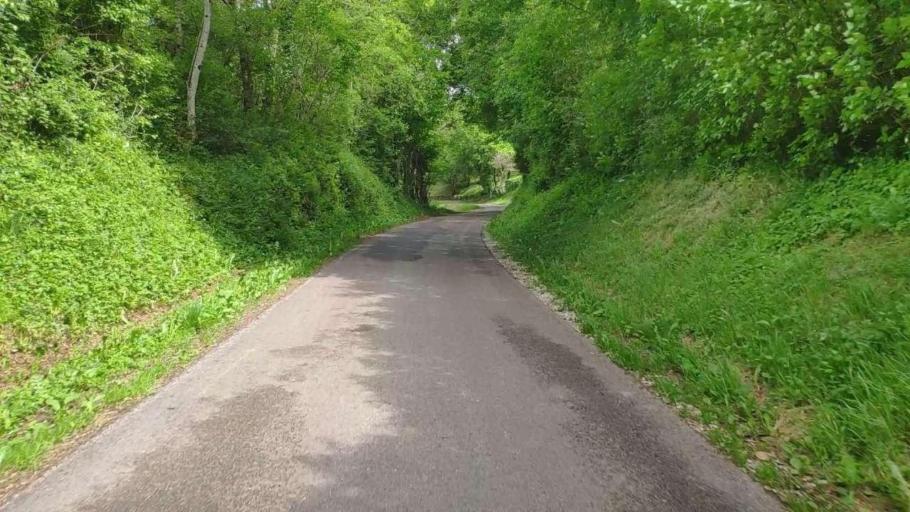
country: FR
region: Franche-Comte
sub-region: Departement du Jura
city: Poligny
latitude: 46.7727
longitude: 5.6250
